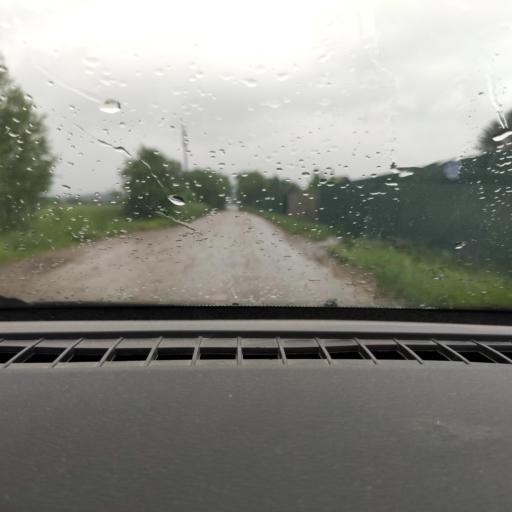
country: RU
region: Perm
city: Perm
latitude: 58.0331
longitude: 56.3616
